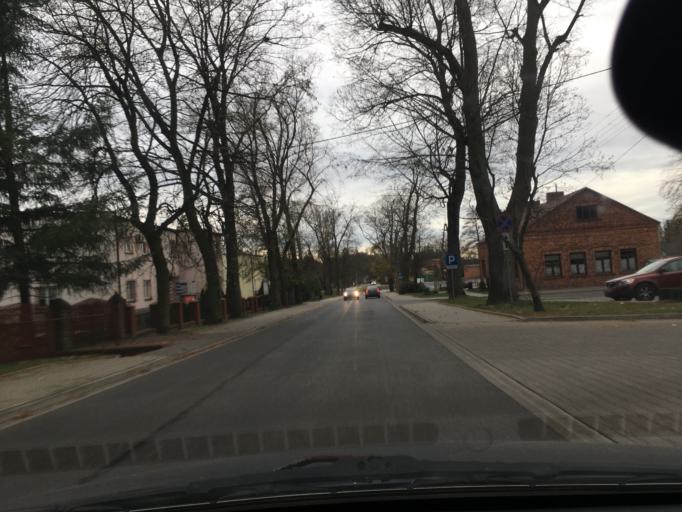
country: PL
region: Masovian Voivodeship
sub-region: Powiat zyrardowski
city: Radziejowice
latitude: 52.0038
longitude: 20.5595
